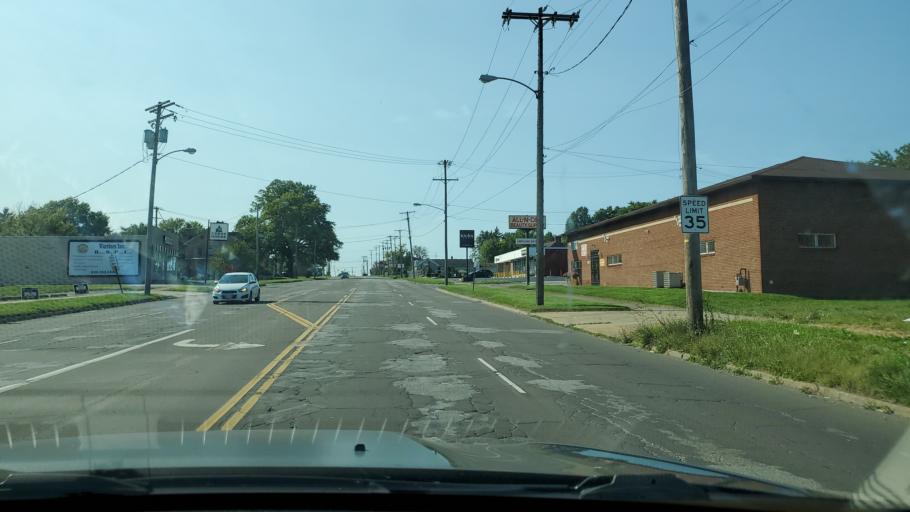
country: US
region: Ohio
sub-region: Mahoning County
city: Youngstown
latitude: 41.0653
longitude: -80.6615
